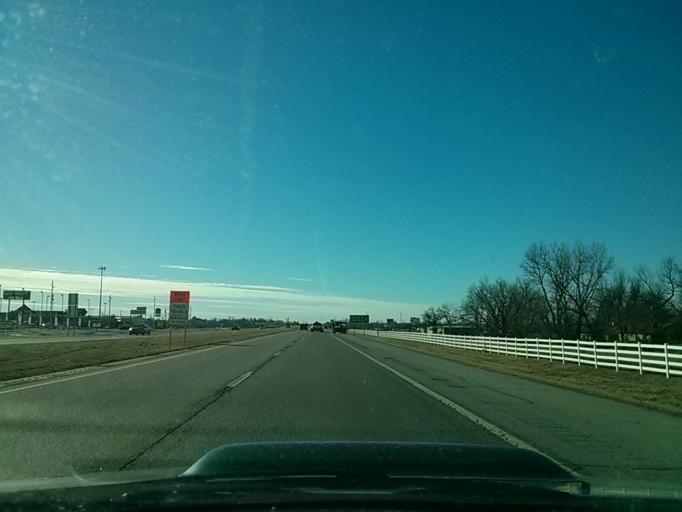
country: US
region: Oklahoma
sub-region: Tulsa County
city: Owasso
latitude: 36.2705
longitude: -95.8487
